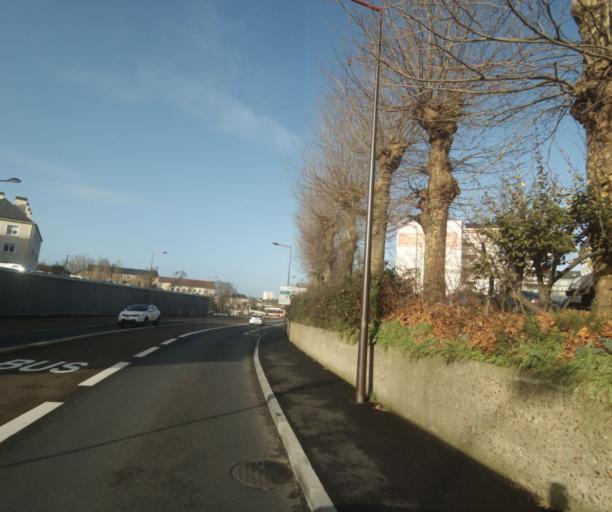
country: FR
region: Pays de la Loire
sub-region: Departement de la Sarthe
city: Le Mans
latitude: 47.9972
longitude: 0.1896
